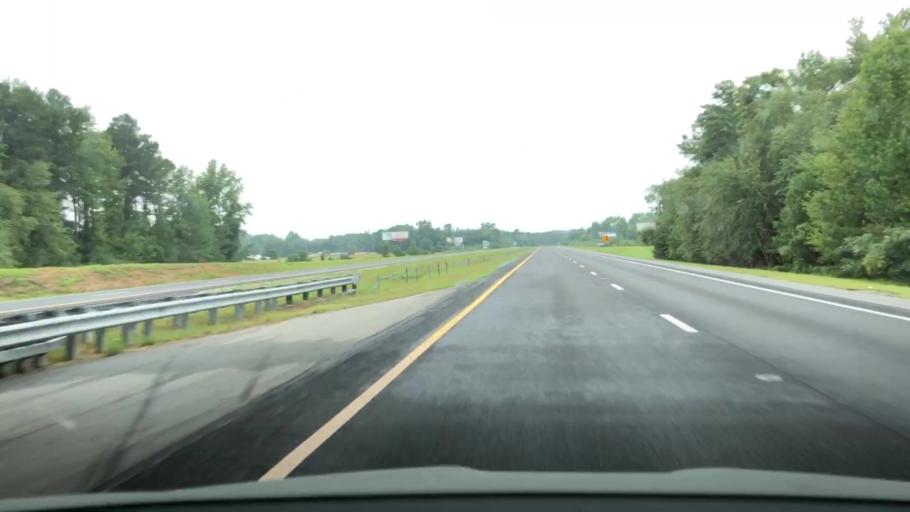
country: US
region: North Carolina
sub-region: Wayne County
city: Fremont
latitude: 35.4953
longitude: -77.9962
